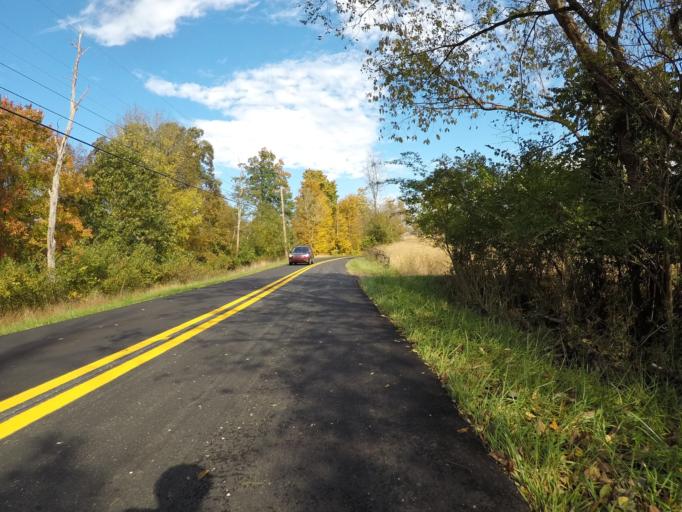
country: US
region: West Virginia
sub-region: Cabell County
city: Huntington
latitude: 38.3743
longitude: -82.4286
